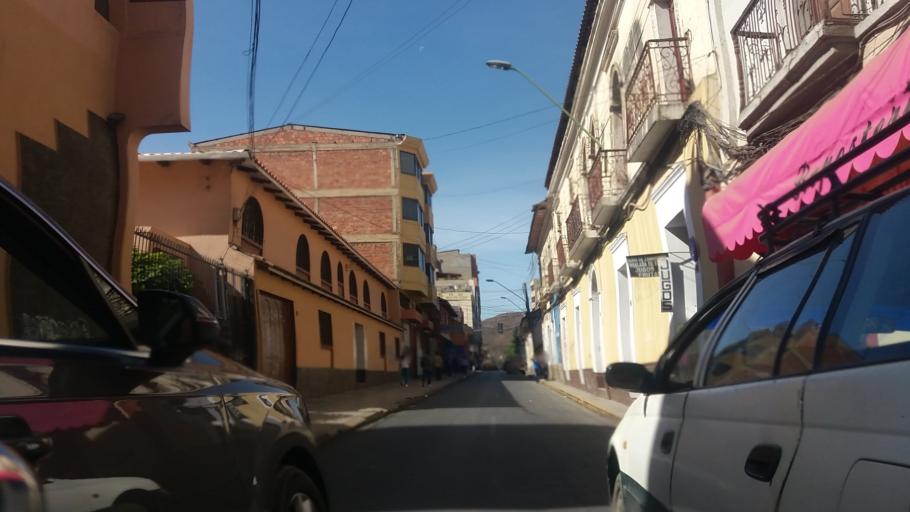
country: BO
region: Cochabamba
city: Cochabamba
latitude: -17.3936
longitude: -66.1529
